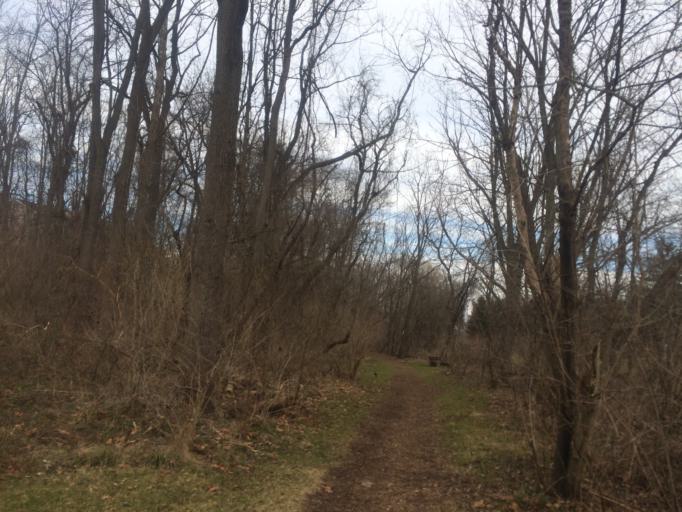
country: US
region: Pennsylvania
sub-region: Lebanon County
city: Annville
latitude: 40.3275
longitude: -76.5006
